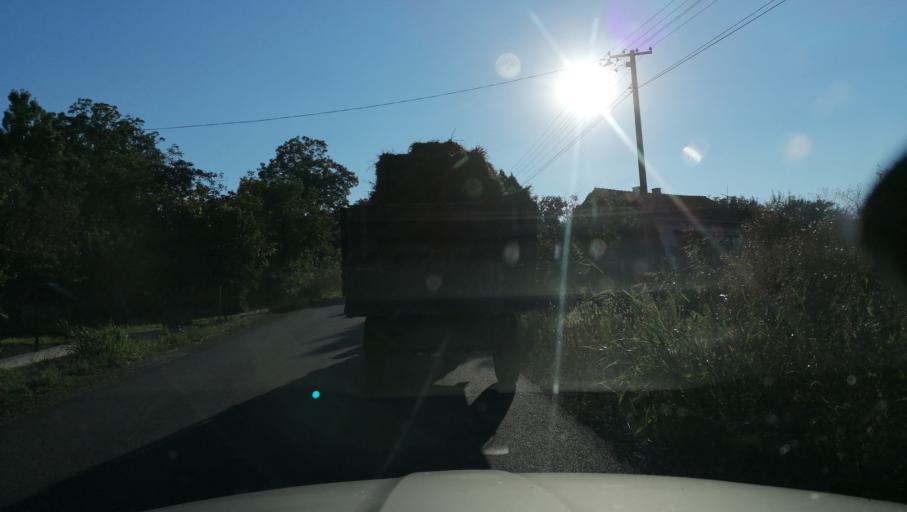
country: RS
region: Central Serbia
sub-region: Sumadijski Okrug
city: Kragujevac
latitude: 44.1072
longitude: 20.8246
